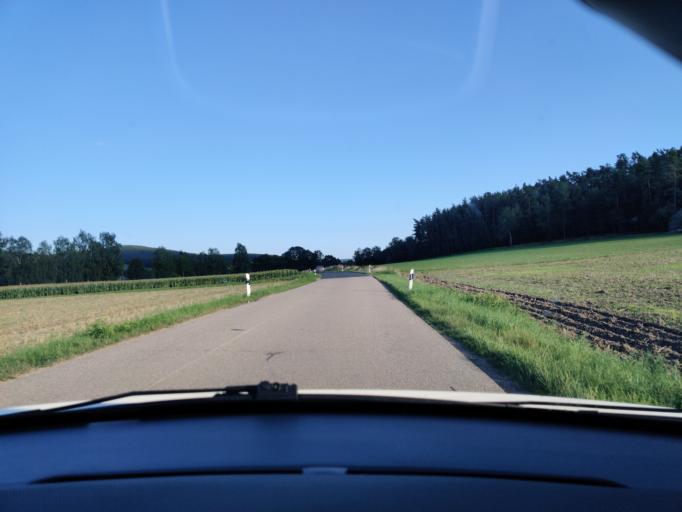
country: DE
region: Bavaria
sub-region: Upper Palatinate
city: Stulln
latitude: 49.4168
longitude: 12.1560
